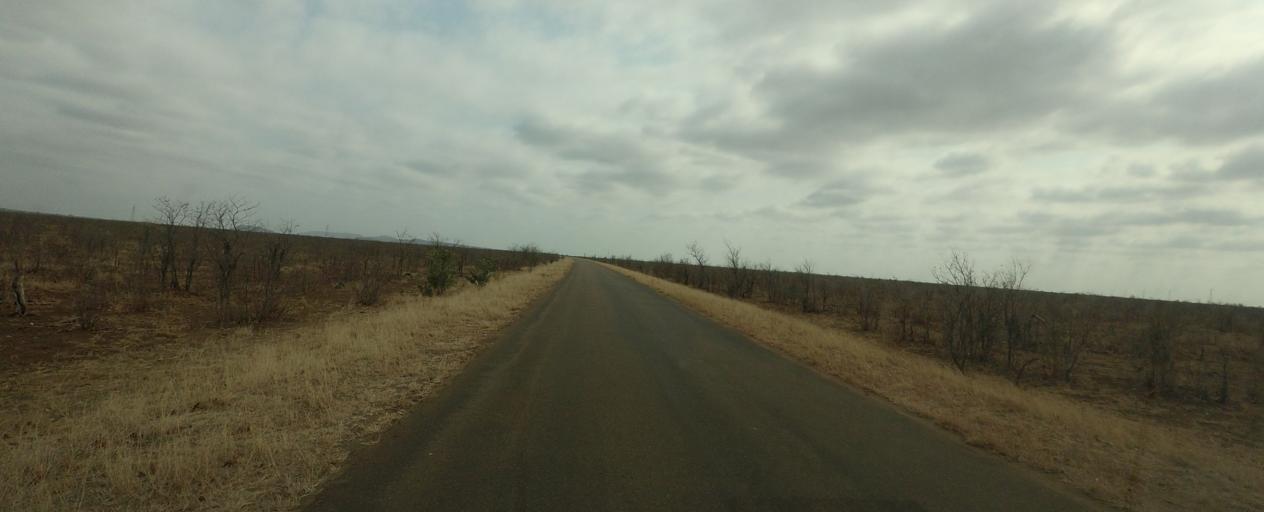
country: ZA
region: Limpopo
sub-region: Vhembe District Municipality
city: Mutale
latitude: -22.6780
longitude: 31.1673
